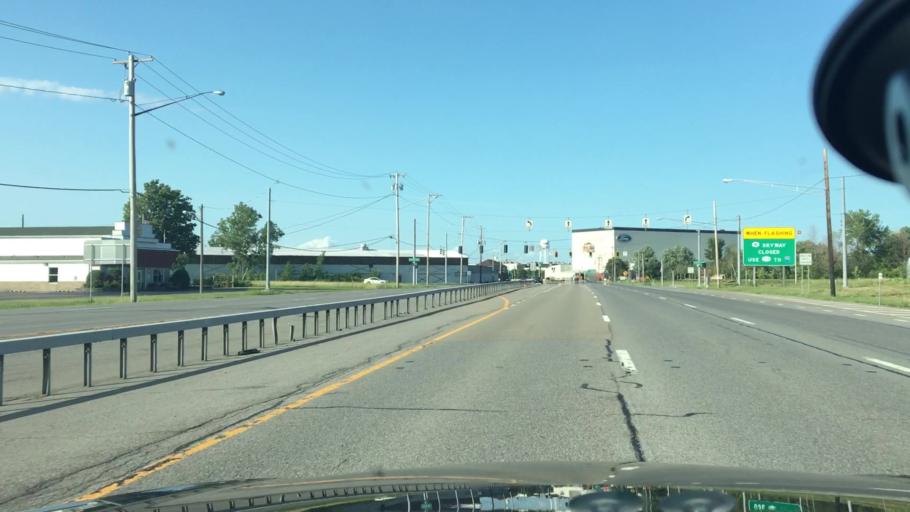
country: US
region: New York
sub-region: Erie County
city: Blasdell
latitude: 42.7809
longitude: -78.8520
